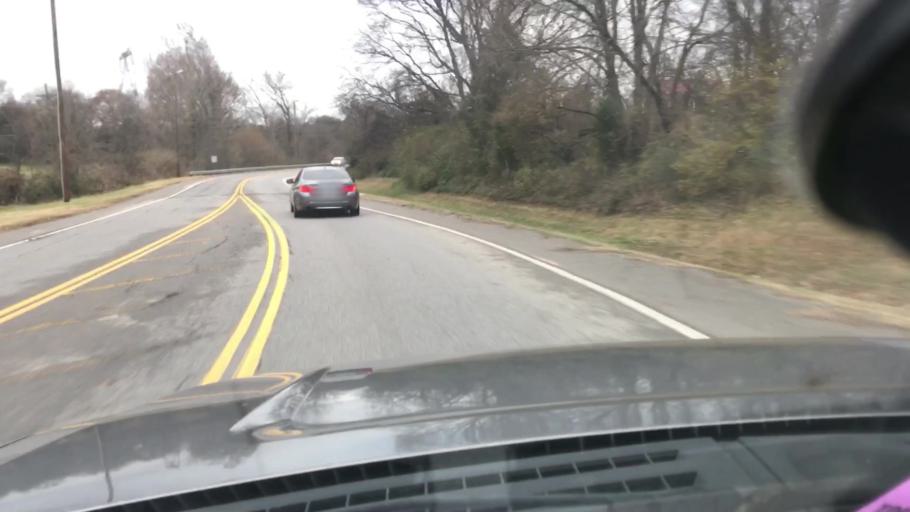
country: US
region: Tennessee
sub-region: Williamson County
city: Brentwood Estates
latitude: 35.9668
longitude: -86.7775
